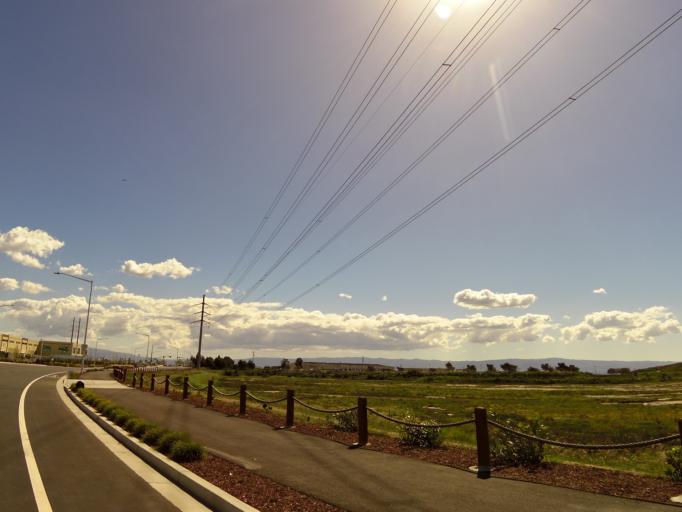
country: US
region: California
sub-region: Santa Clara County
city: Milpitas
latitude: 37.4586
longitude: -121.9263
